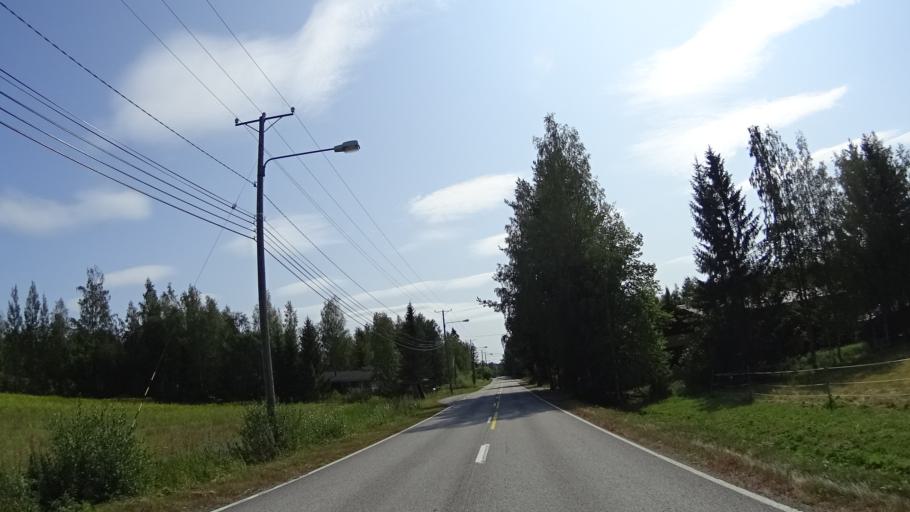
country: FI
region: Pirkanmaa
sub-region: Ylae-Pirkanmaa
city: Maenttae
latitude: 61.9144
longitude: 24.7765
